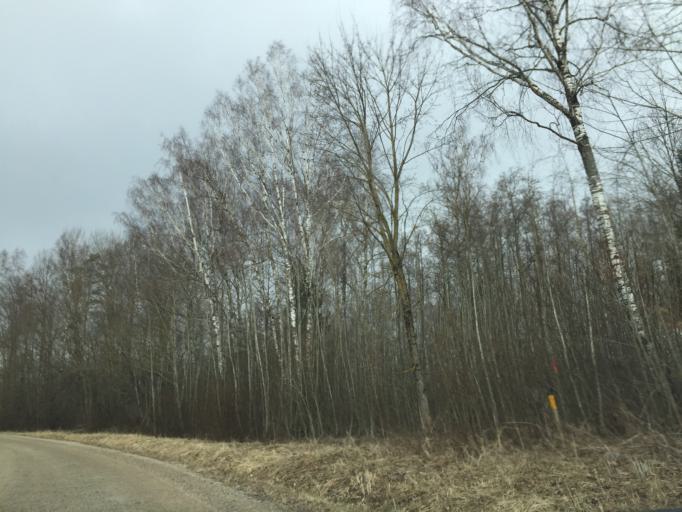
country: LV
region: Ilukste
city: Ilukste
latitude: 56.0207
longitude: 26.2357
